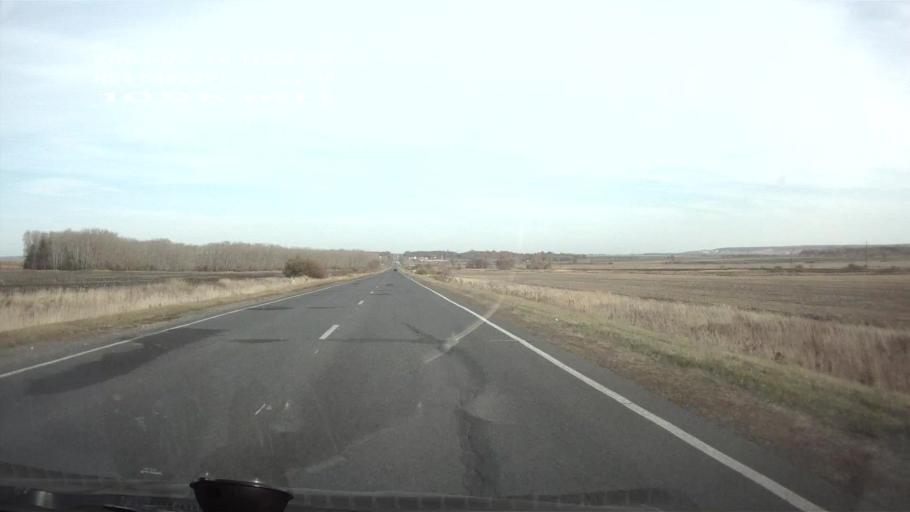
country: RU
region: Mordoviya
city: Atyashevo
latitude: 54.5482
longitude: 45.9511
